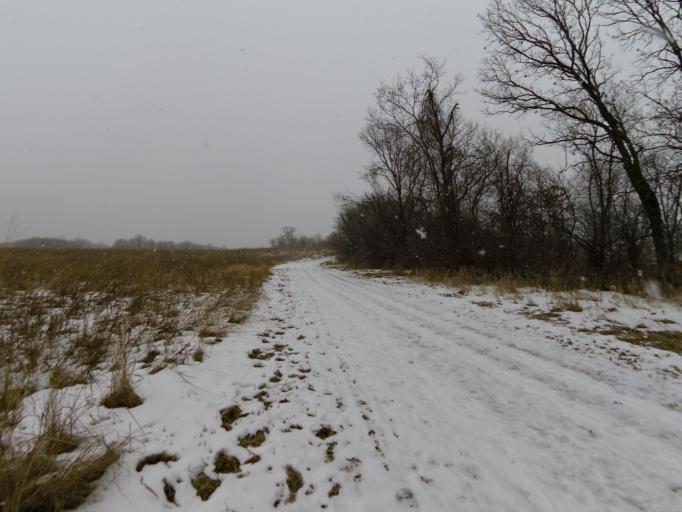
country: US
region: Minnesota
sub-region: Washington County
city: Lake Elmo
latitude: 44.9815
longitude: -92.9131
